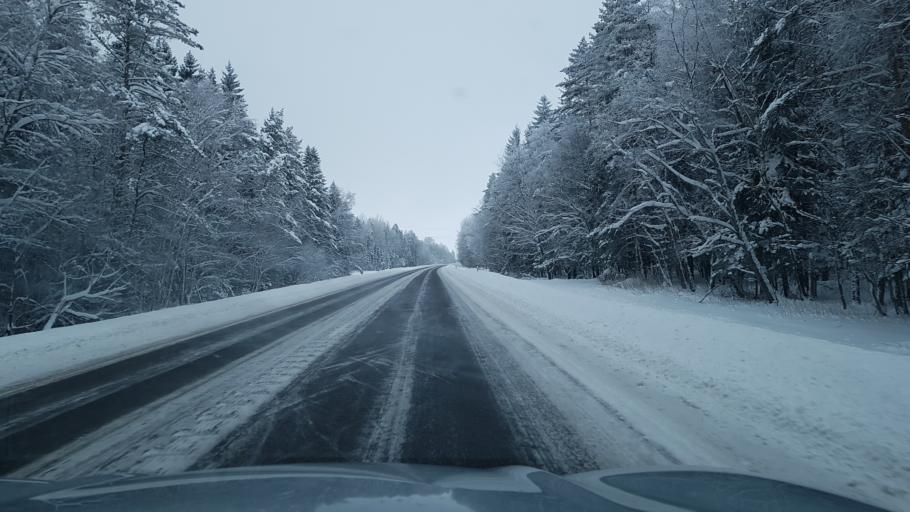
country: EE
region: Ida-Virumaa
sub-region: Johvi vald
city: Johvi
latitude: 59.3028
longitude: 27.3948
